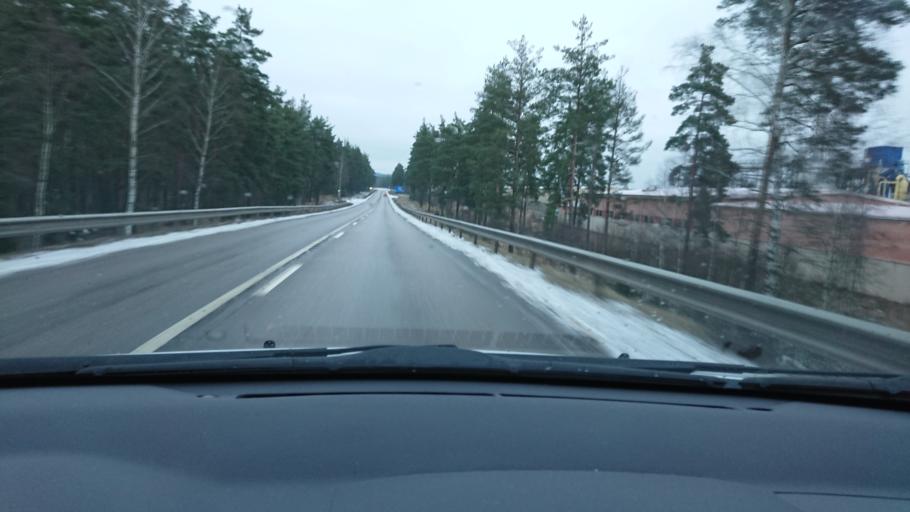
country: SE
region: Kalmar
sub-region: Hultsfreds Kommun
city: Hultsfred
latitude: 57.5056
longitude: 15.8286
